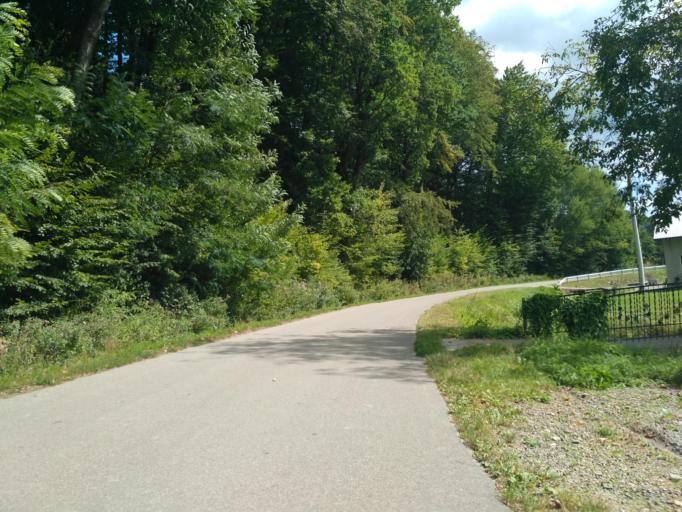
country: PL
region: Subcarpathian Voivodeship
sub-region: Powiat rzeszowski
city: Dynow
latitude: 49.7737
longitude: 22.2516
